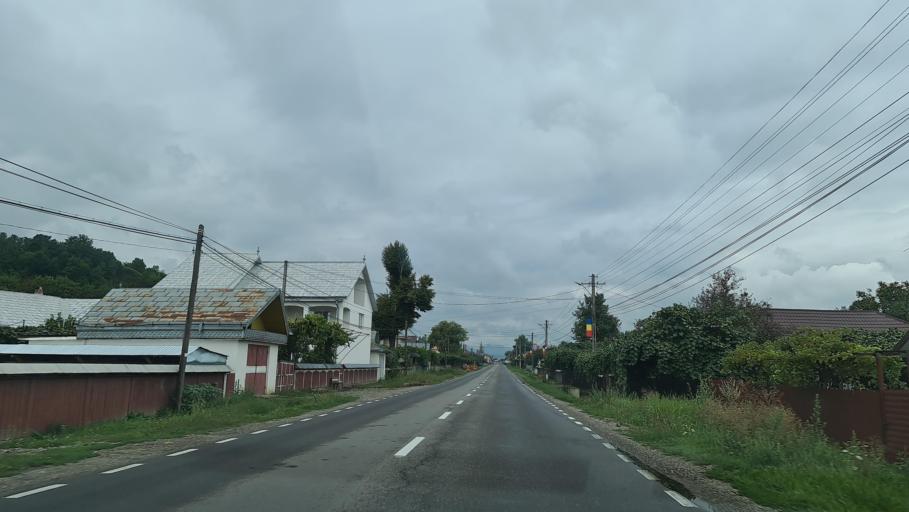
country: RO
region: Neamt
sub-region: Comuna Borlesti
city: Ruseni
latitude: 46.7998
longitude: 26.5355
